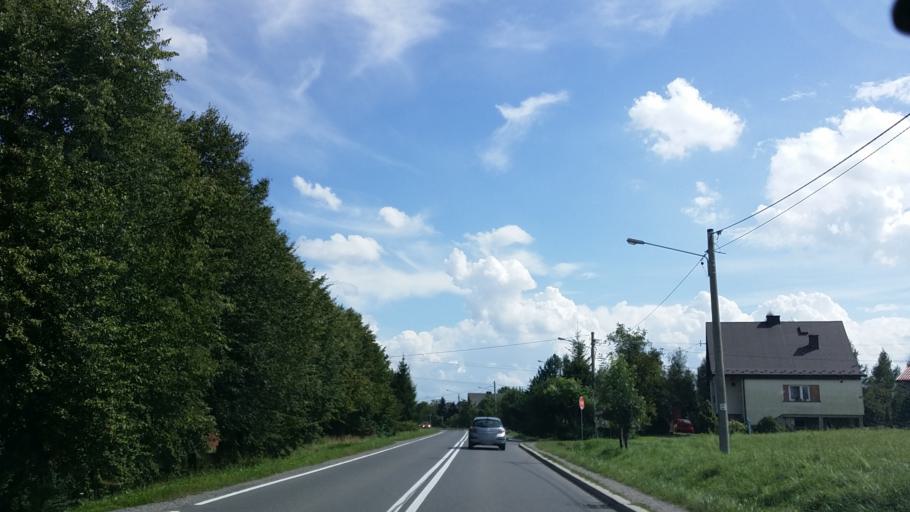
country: PL
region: Lesser Poland Voivodeship
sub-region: Powiat myslenicki
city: Dobczyce
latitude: 49.9133
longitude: 20.0930
